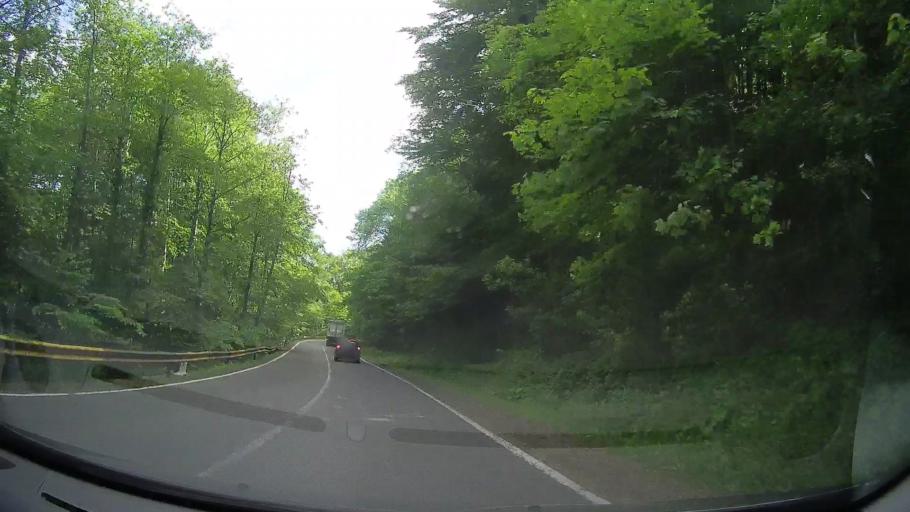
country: RO
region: Prahova
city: Maneciu
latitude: 45.3755
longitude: 25.9290
